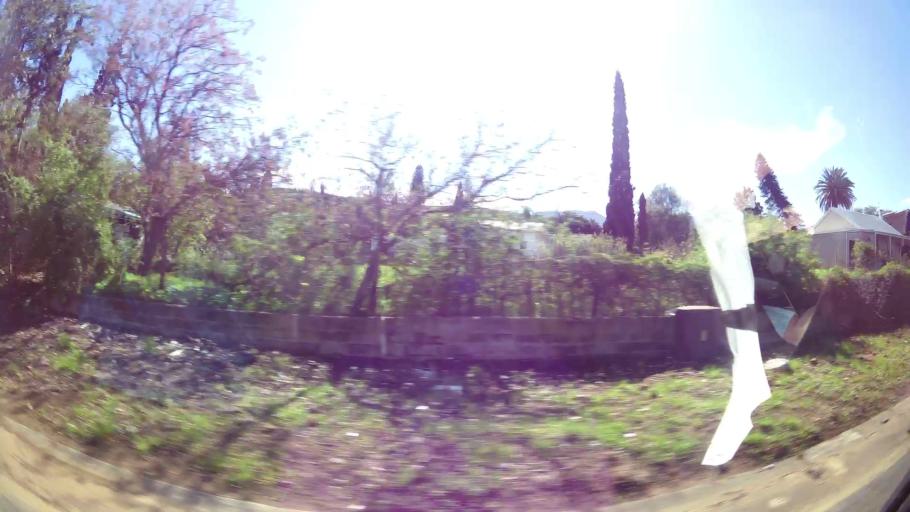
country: ZA
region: Western Cape
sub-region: Cape Winelands District Municipality
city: Ashton
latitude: -33.8320
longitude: 20.0569
